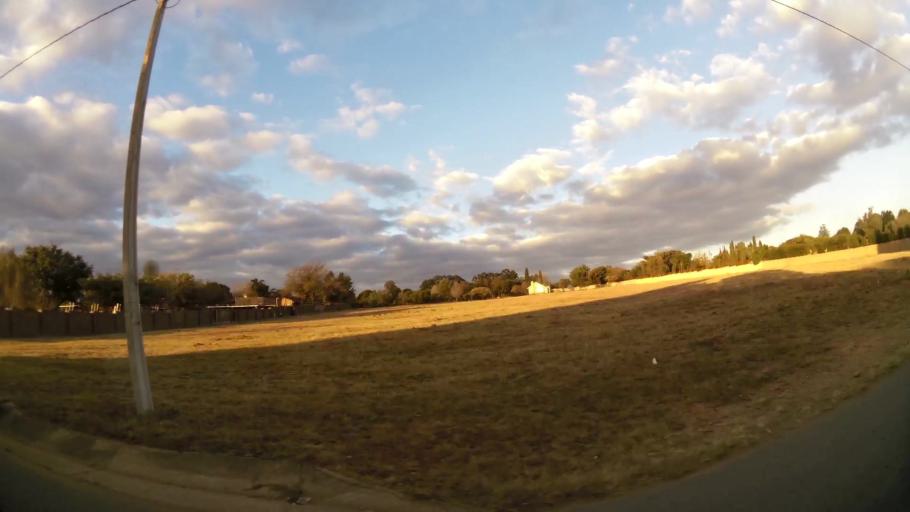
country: ZA
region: Gauteng
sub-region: City of Johannesburg Metropolitan Municipality
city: Midrand
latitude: -26.0011
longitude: 28.1514
